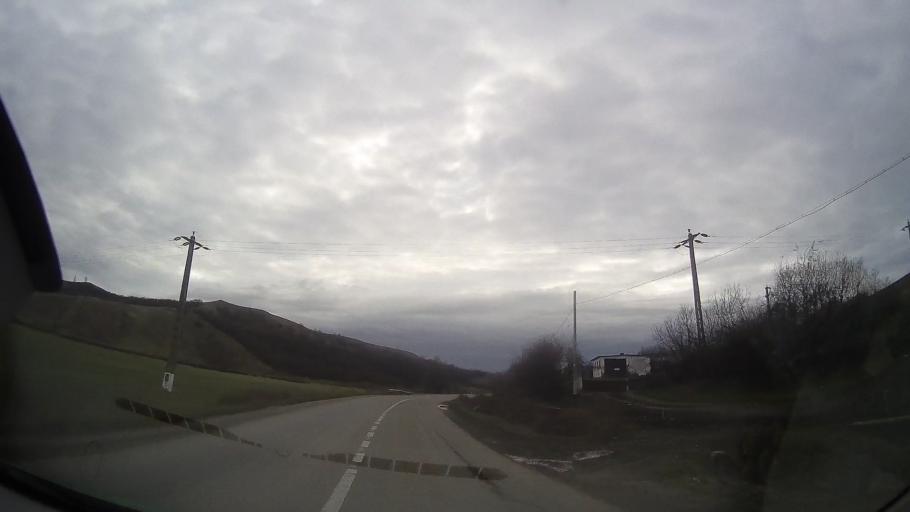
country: RO
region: Bistrita-Nasaud
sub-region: Comuna Budesti
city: Budesti
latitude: 46.8668
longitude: 24.2465
